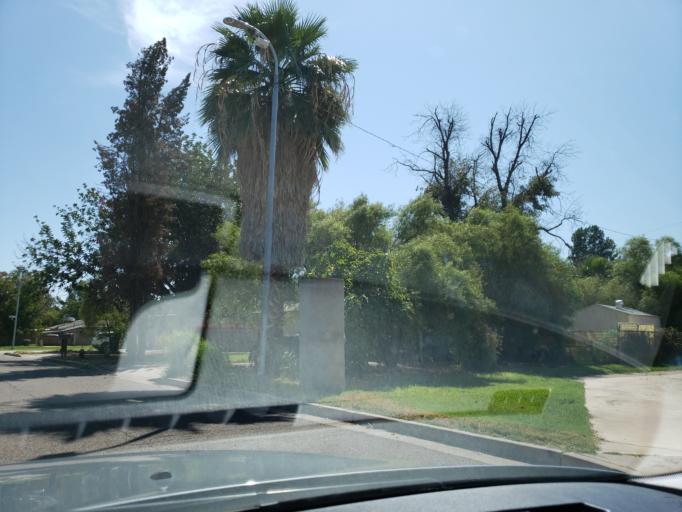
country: US
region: Arizona
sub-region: Maricopa County
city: Glendale
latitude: 33.5580
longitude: -112.0983
